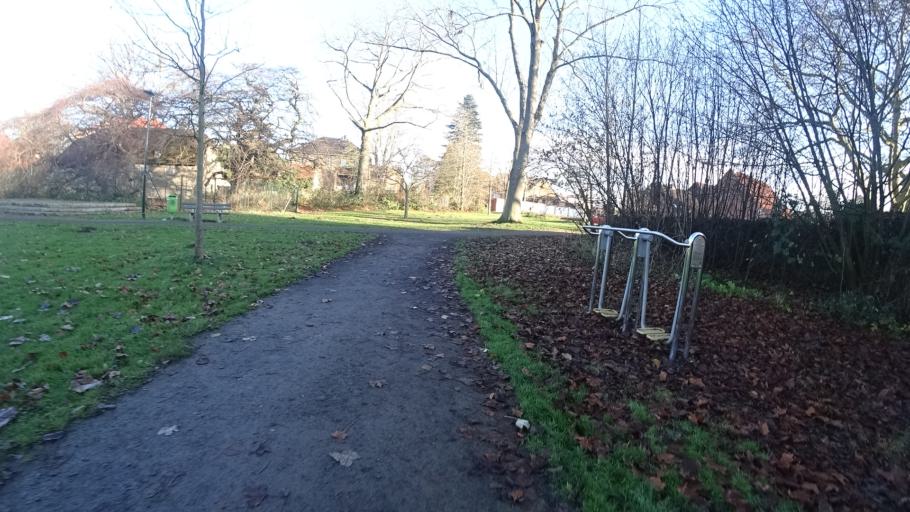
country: DE
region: Lower Saxony
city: Lauenau
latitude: 52.2755
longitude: 9.3674
